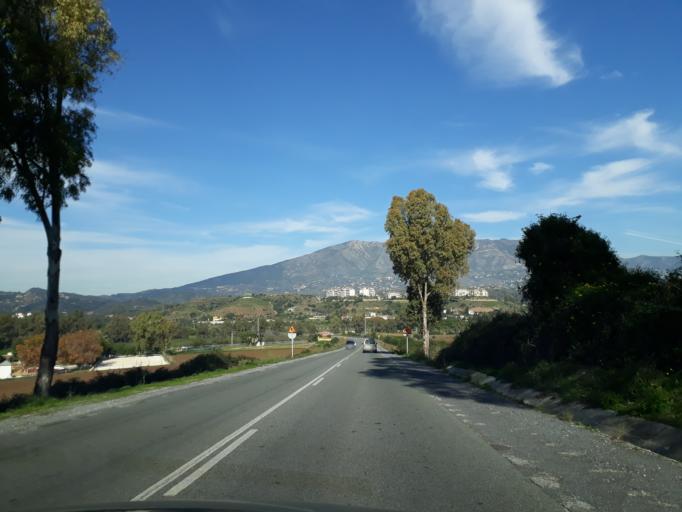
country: ES
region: Andalusia
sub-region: Provincia de Malaga
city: Fuengirola
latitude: 36.5391
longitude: -4.6876
